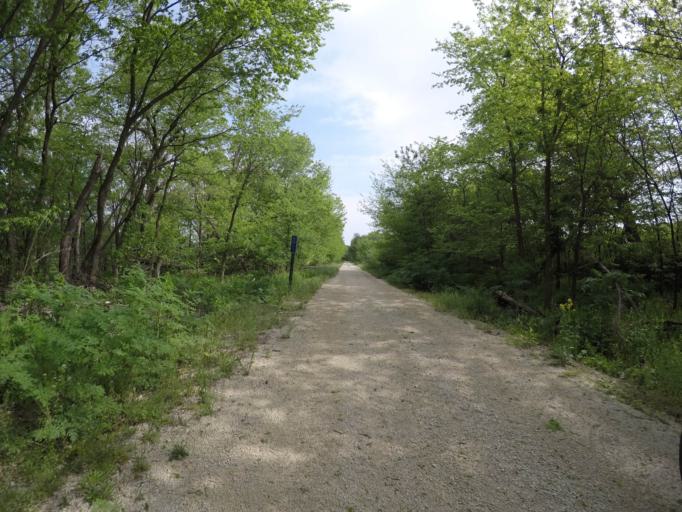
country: US
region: Nebraska
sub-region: Gage County
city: Wymore
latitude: 40.0140
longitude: -96.5933
